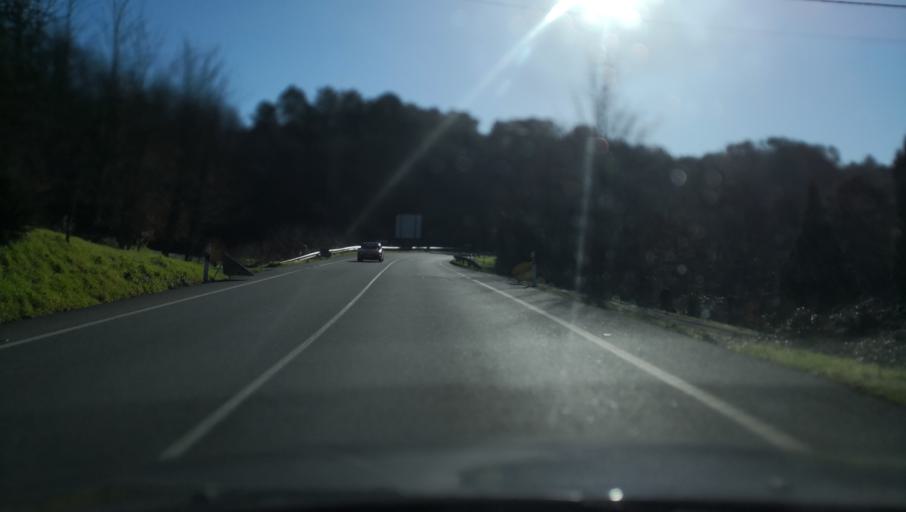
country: ES
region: Galicia
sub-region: Provincia da Coruna
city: Ribeira
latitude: 42.7716
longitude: -8.3995
